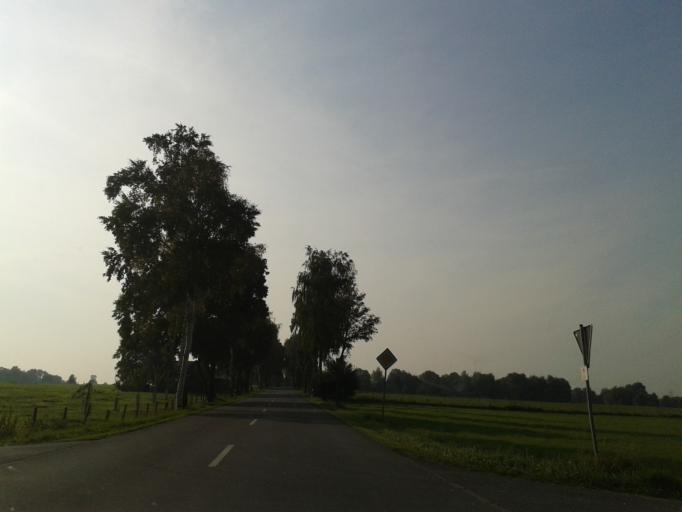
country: DE
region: North Rhine-Westphalia
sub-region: Regierungsbezirk Detmold
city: Salzkotten
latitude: 51.7269
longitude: 8.6271
